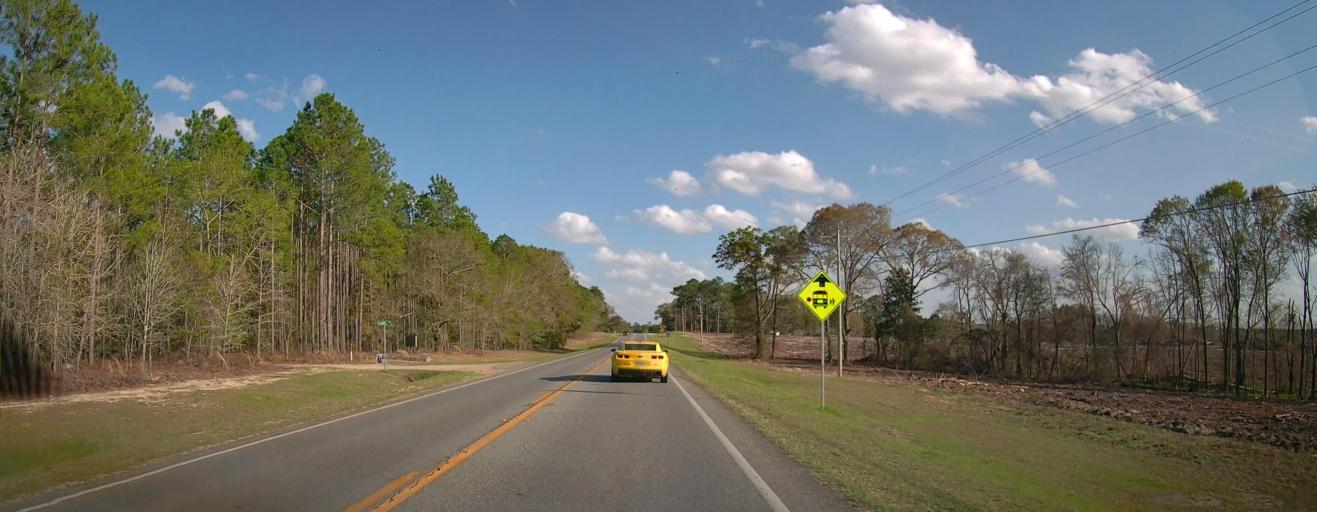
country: US
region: Georgia
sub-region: Toombs County
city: Lyons
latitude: 32.1903
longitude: -82.3048
